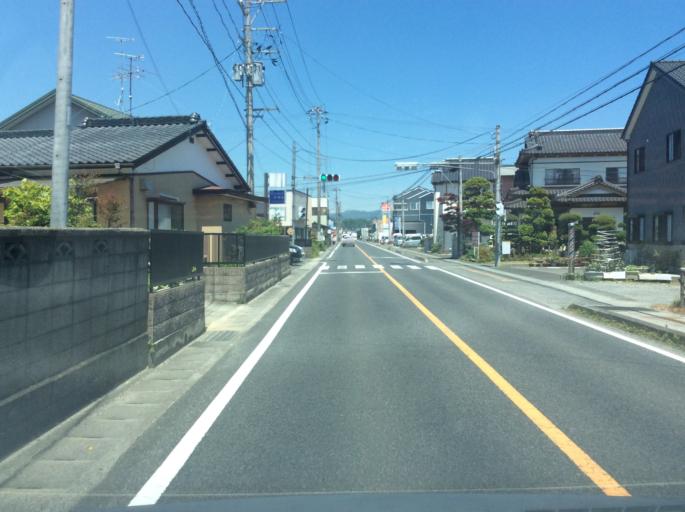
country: JP
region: Fukushima
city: Iwaki
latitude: 37.0779
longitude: 140.8807
